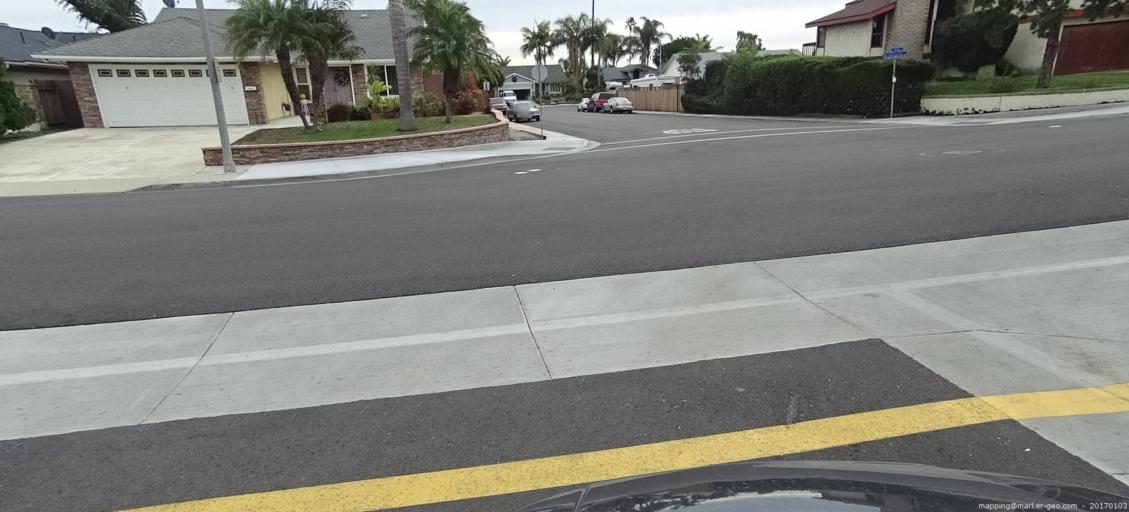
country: US
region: California
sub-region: Orange County
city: Dana Point
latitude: 33.4633
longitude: -117.6665
